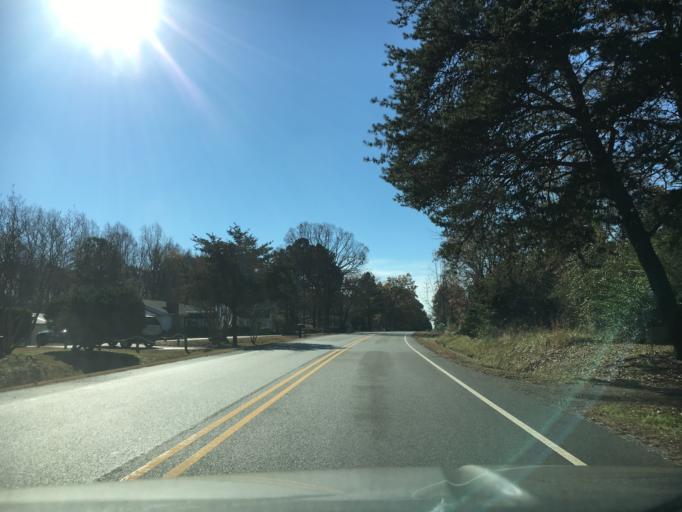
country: US
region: Virginia
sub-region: Cumberland County
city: Cumberland
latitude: 37.5219
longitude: -78.2075
